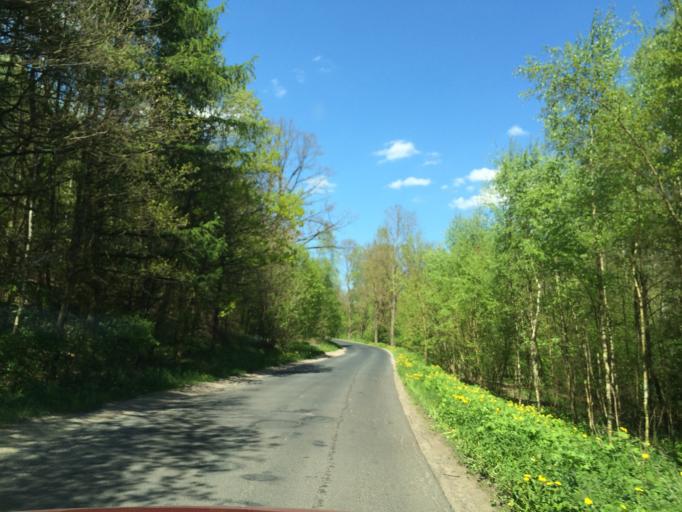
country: PL
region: Warmian-Masurian Voivodeship
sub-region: Powiat ilawski
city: Lubawa
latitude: 53.4007
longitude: 19.7457
